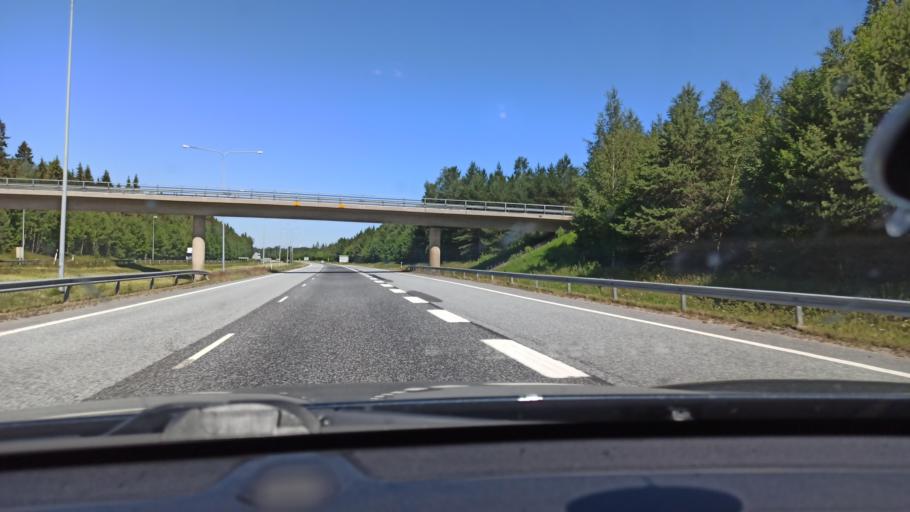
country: FI
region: Ostrobothnia
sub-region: Vaasa
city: Ristinummi
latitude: 63.0575
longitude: 21.7118
